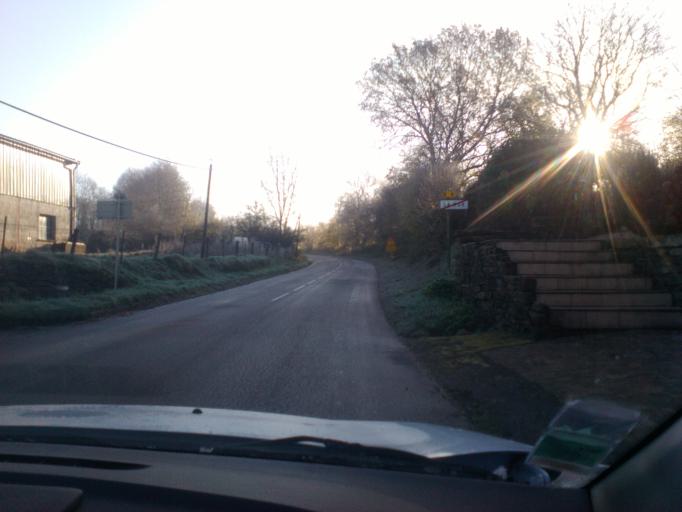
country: FR
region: Lorraine
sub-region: Departement des Vosges
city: Darnieulles
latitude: 48.1587
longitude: 6.2306
